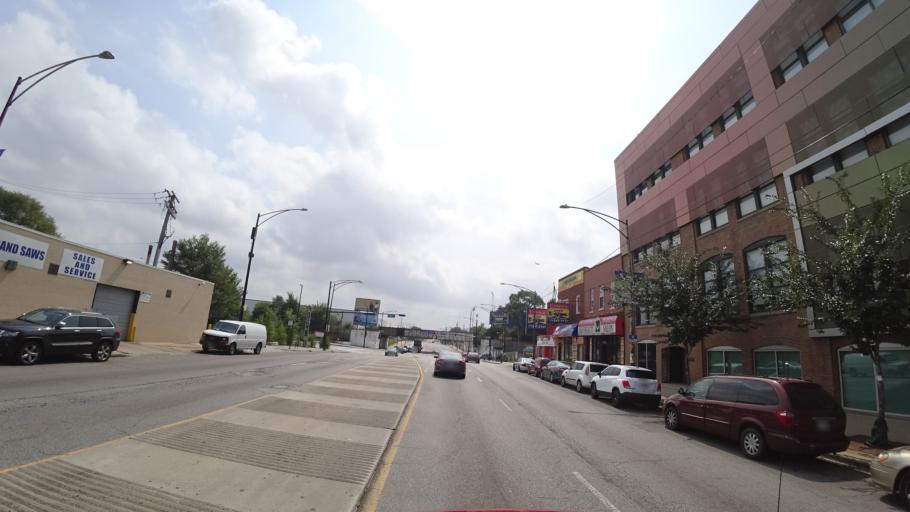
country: US
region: Illinois
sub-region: Cook County
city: Chicago
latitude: 41.8456
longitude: -87.6855
